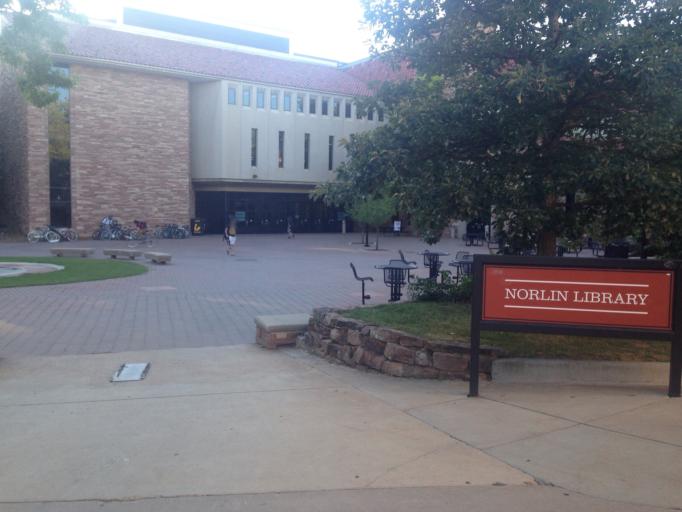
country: US
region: Colorado
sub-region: Boulder County
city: Boulder
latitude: 40.0085
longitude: -105.2698
